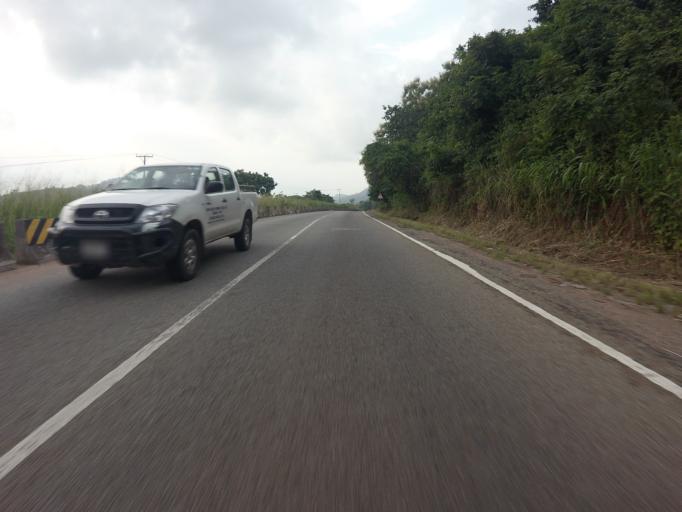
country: GH
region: Volta
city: Ho
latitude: 6.6351
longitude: 0.4655
